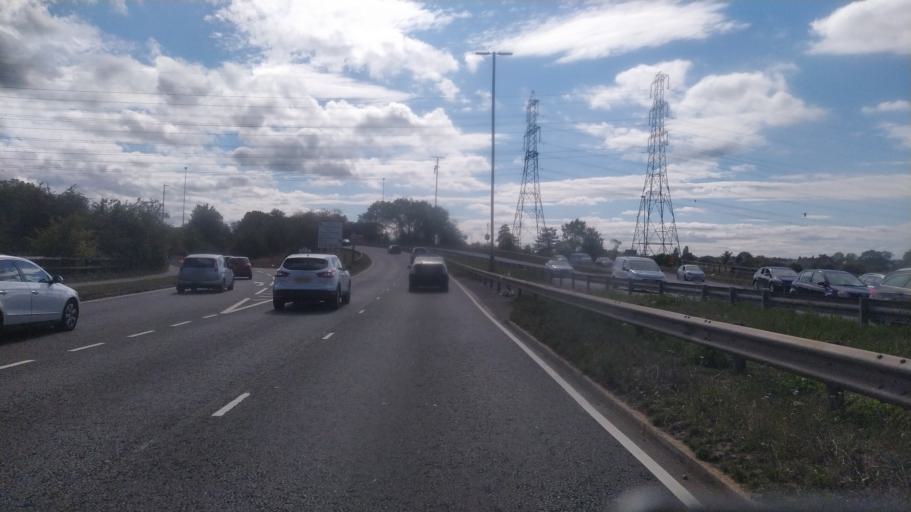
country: GB
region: England
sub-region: Hampshire
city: Totton
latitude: 50.9207
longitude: -1.4769
